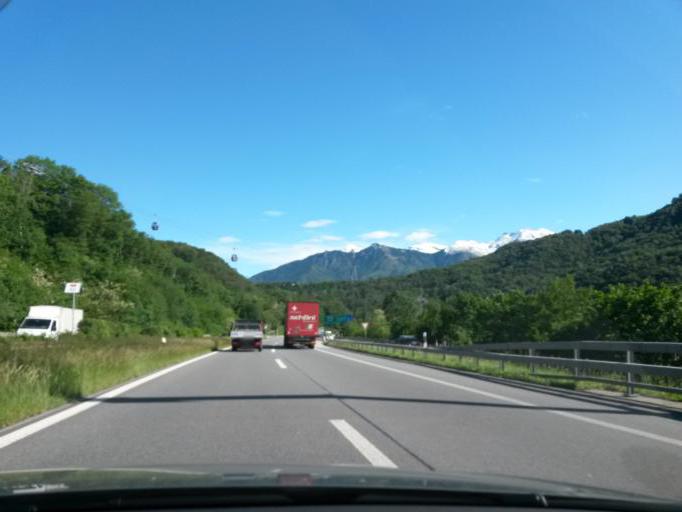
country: CH
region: Ticino
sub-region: Bellinzona District
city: Cadenazzo
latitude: 46.1252
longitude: 8.9190
